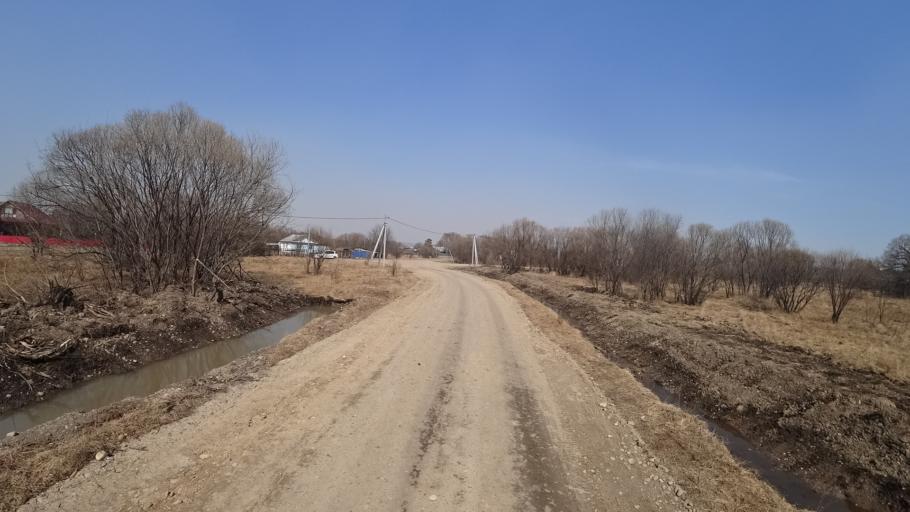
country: RU
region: Amur
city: Novobureyskiy
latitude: 49.7770
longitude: 129.8486
